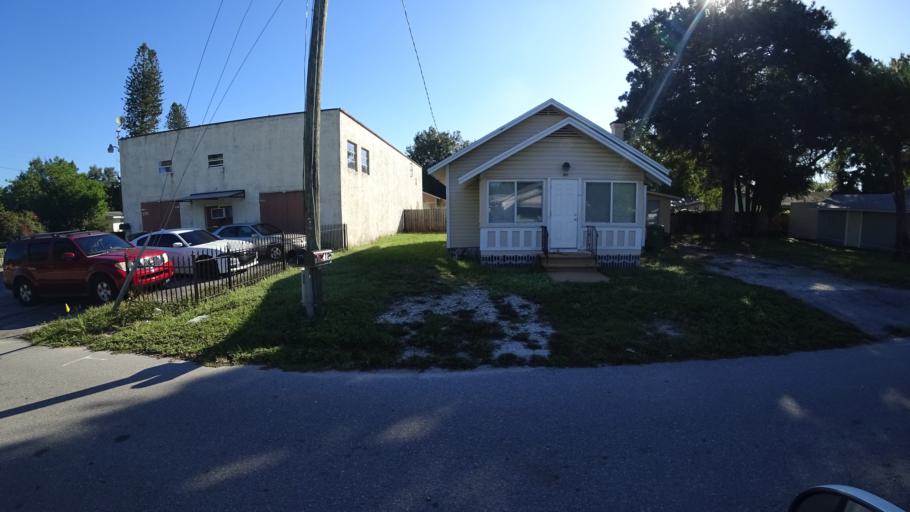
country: US
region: Florida
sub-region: Manatee County
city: West Samoset
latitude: 27.4805
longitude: -82.5692
